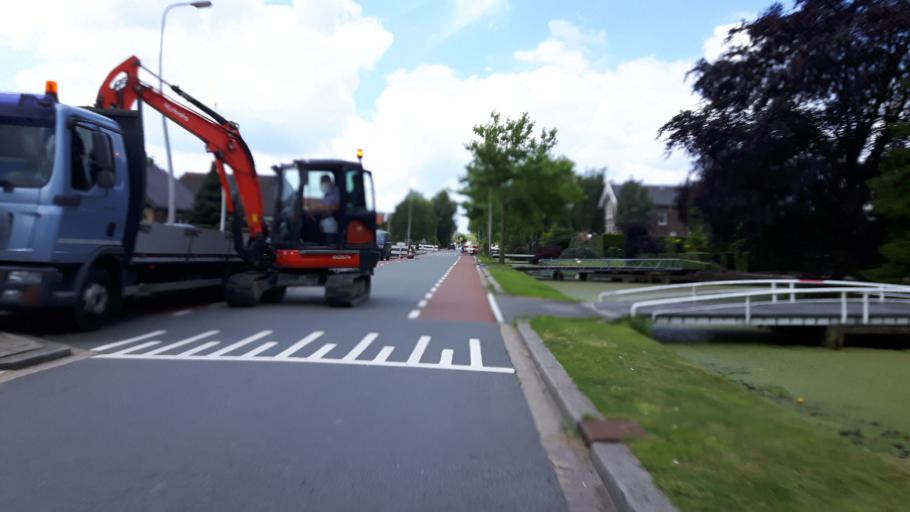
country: NL
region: South Holland
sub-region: Gemeente Boskoop
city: Boskoop
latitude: 52.0732
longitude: 4.6831
